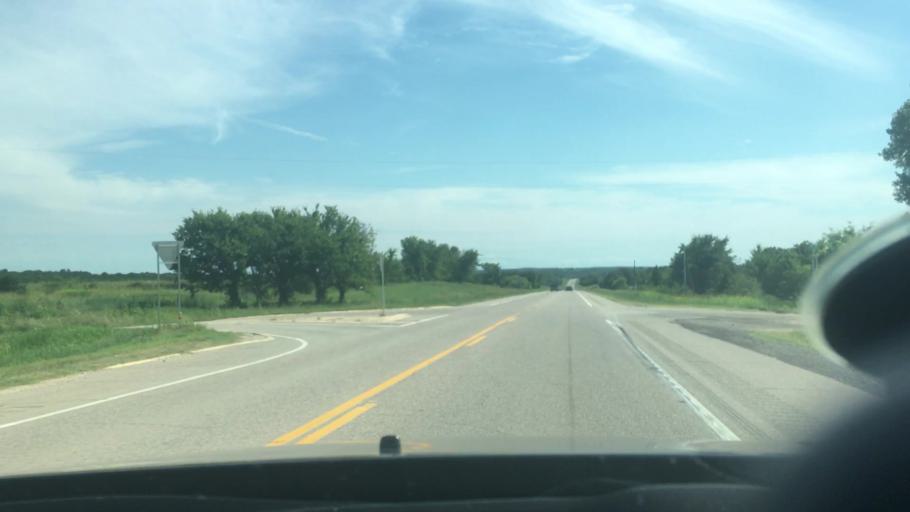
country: US
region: Oklahoma
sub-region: Seminole County
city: Maud
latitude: 35.0874
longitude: -96.6789
